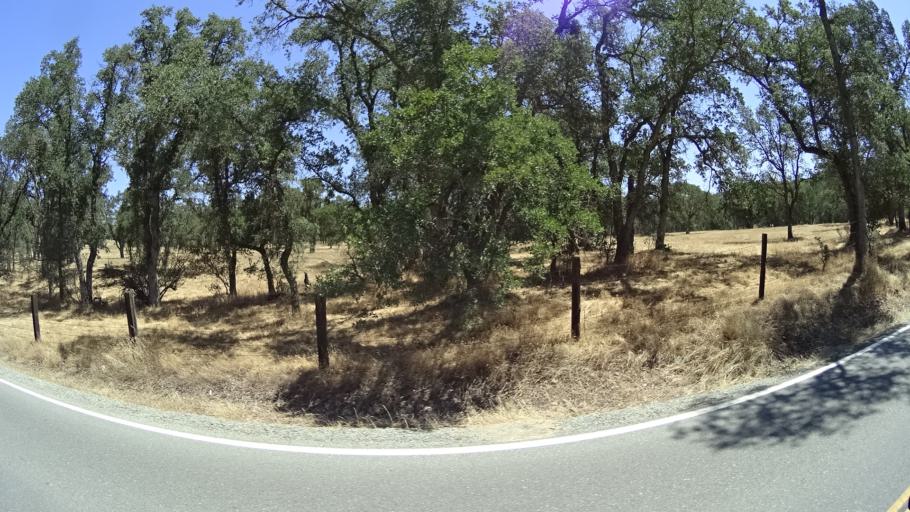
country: US
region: California
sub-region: Calaveras County
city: Rancho Calaveras
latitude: 38.1367
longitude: -120.8807
